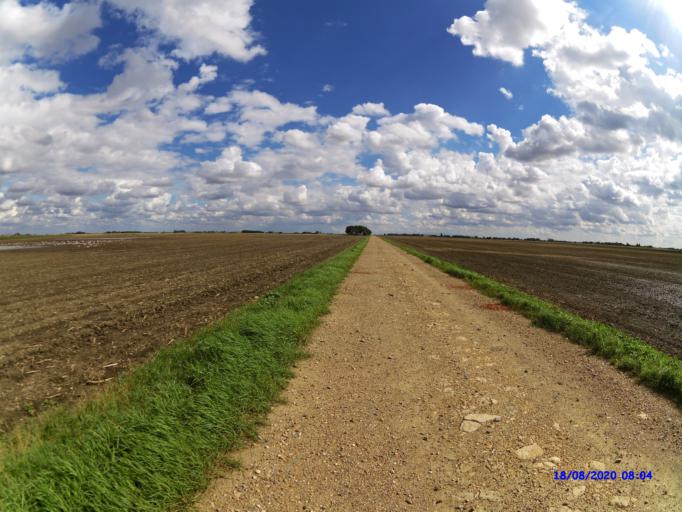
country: GB
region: England
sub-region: Cambridgeshire
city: Whittlesey
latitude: 52.5141
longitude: -0.0857
